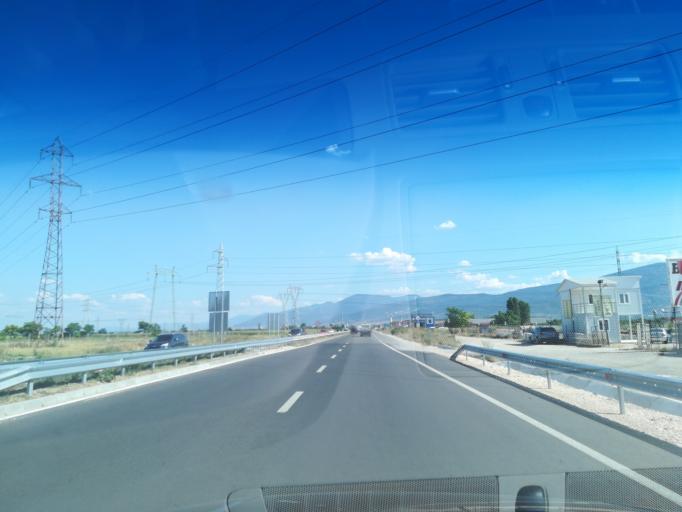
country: BG
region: Plovdiv
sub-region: Obshtina Plovdiv
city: Plovdiv
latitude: 42.0976
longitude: 24.7892
